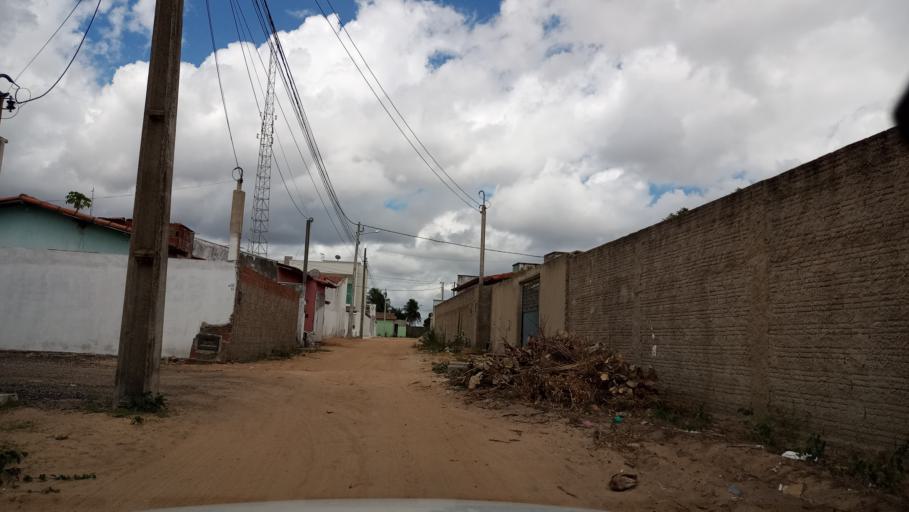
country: BR
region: Rio Grande do Norte
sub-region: Joao Camara
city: Joao Camara
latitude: -5.5349
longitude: -35.8113
